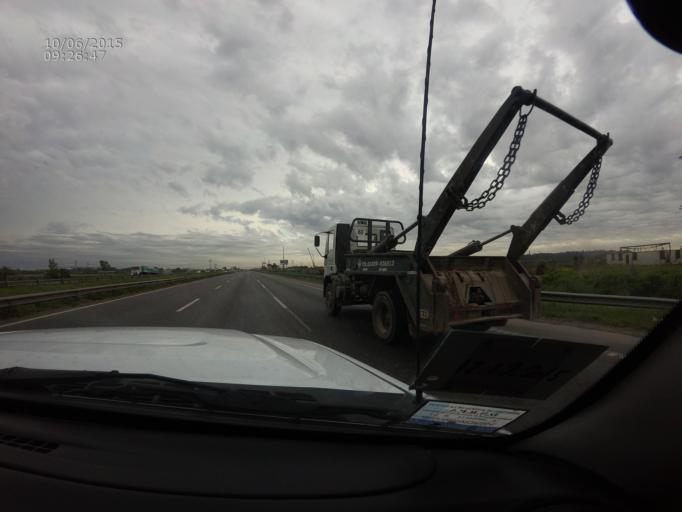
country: AR
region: Buenos Aires
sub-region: Partido de Campana
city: Campana
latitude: -34.1735
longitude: -58.9830
